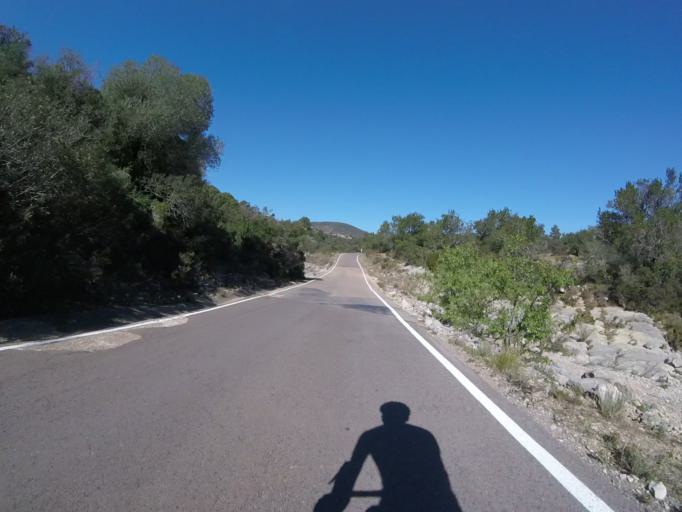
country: ES
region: Valencia
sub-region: Provincia de Castello
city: Santa Magdalena de Pulpis
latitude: 40.3712
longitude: 0.2739
